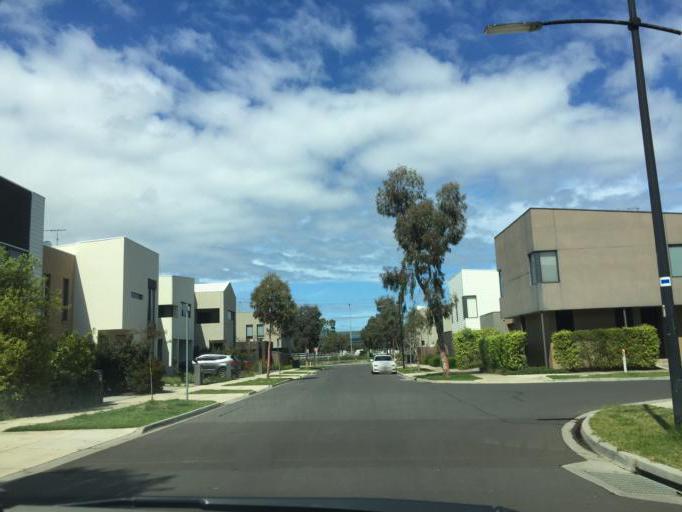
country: AU
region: Victoria
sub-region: Maribyrnong
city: West Footscray
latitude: -37.7999
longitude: 144.8832
